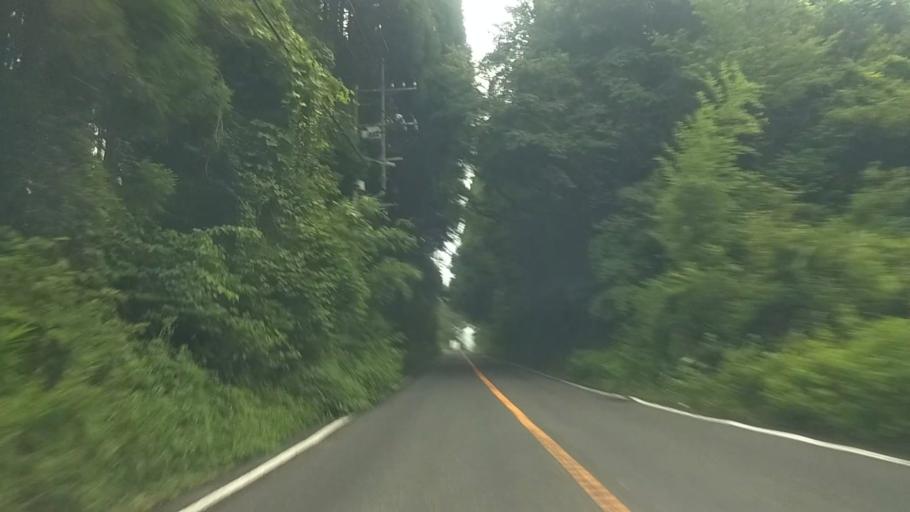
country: JP
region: Chiba
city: Kawaguchi
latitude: 35.2329
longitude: 140.0730
